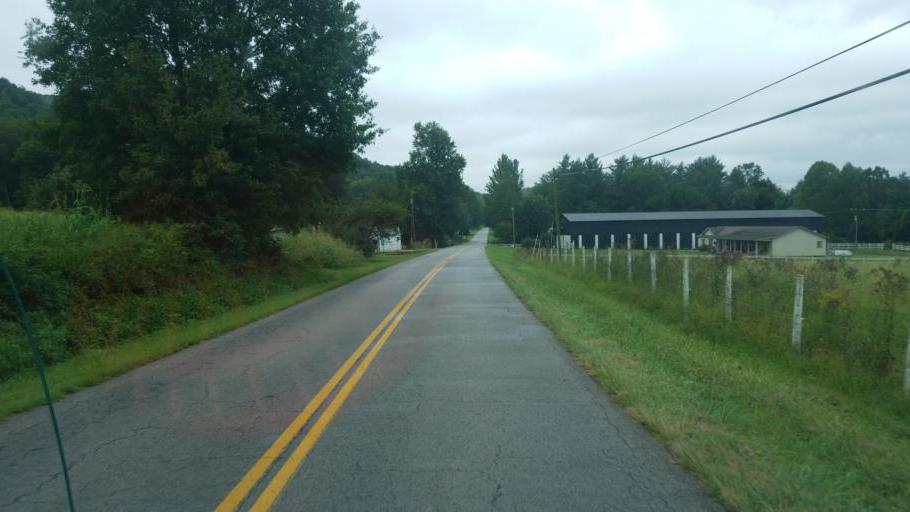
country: US
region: Kentucky
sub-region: Rowan County
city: Morehead
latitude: 38.3375
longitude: -83.5374
